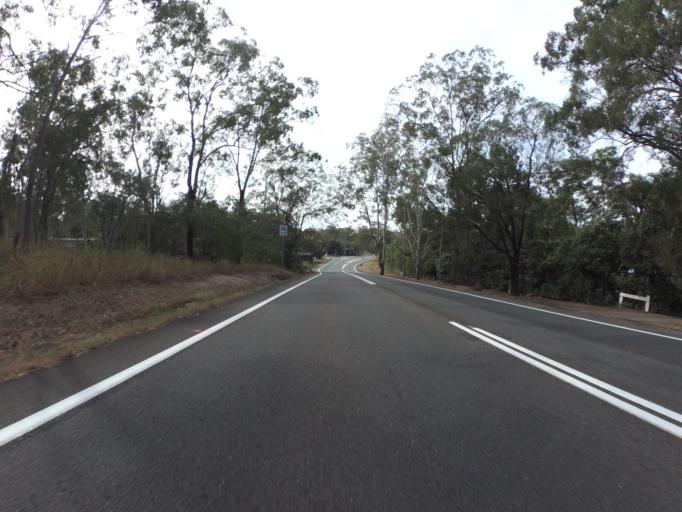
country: AU
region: Queensland
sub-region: Brisbane
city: Pullenvale
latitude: -27.5310
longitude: 152.9088
